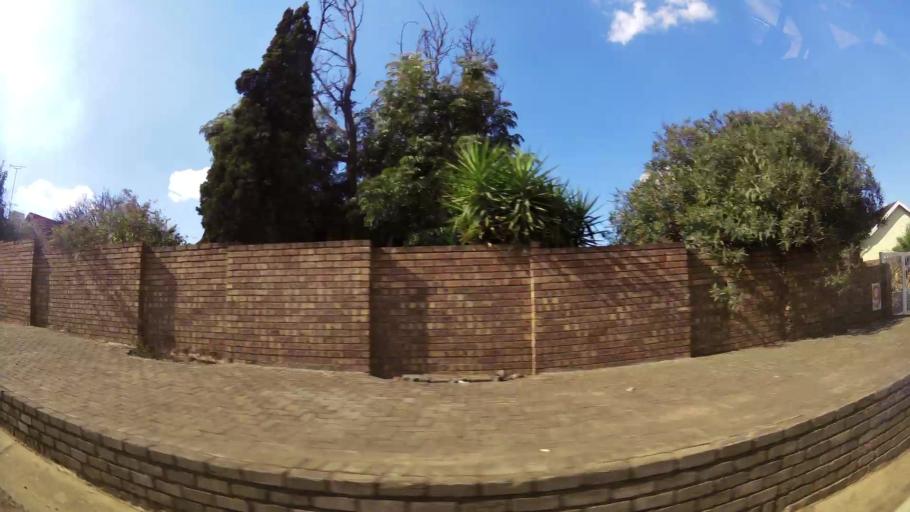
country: ZA
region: Mpumalanga
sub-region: Nkangala District Municipality
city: Witbank
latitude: -25.9279
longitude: 29.2364
